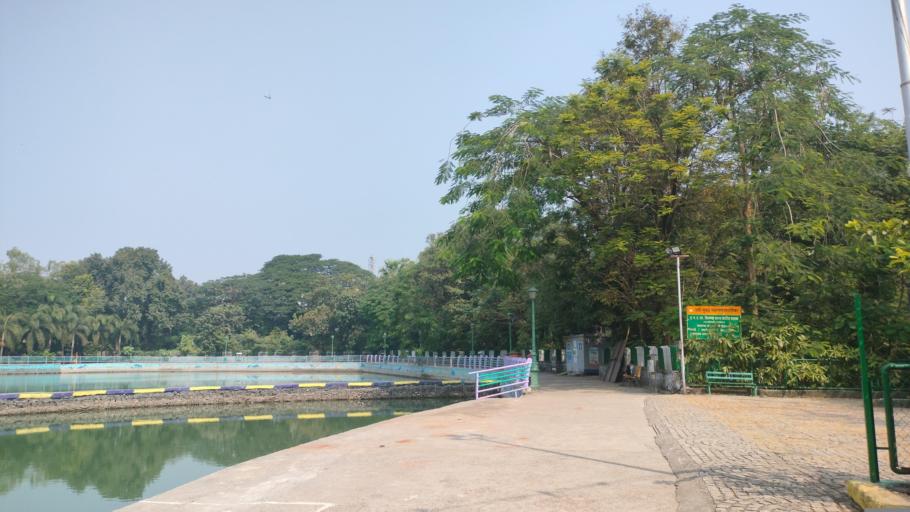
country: IN
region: Maharashtra
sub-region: Thane
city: Artist Village
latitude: 19.0216
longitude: 73.0379
